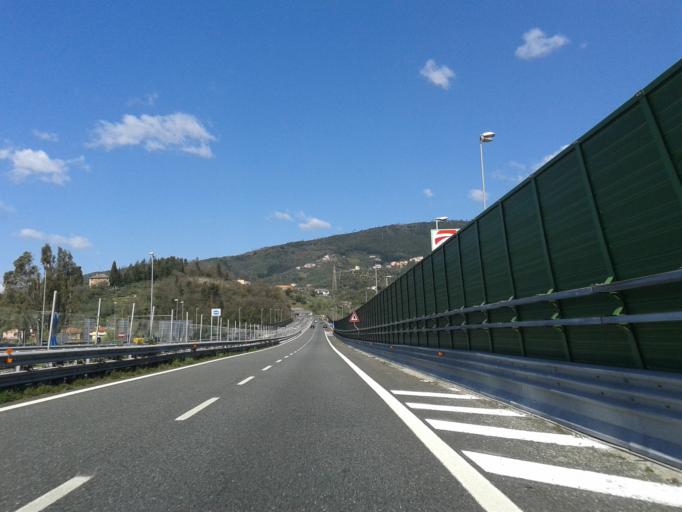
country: IT
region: Liguria
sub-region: Provincia di Genova
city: Sestri Levante
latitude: 44.2750
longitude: 9.4208
